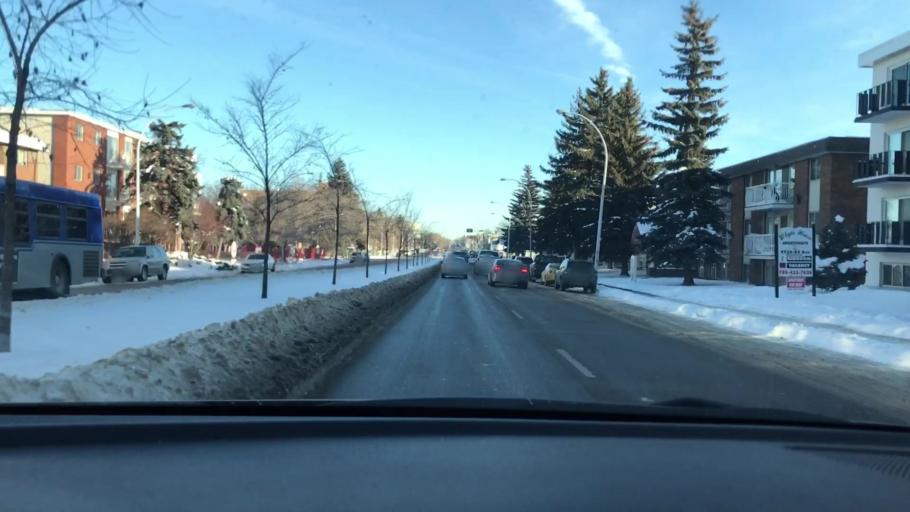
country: CA
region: Alberta
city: Edmonton
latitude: 53.5180
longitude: -113.4824
